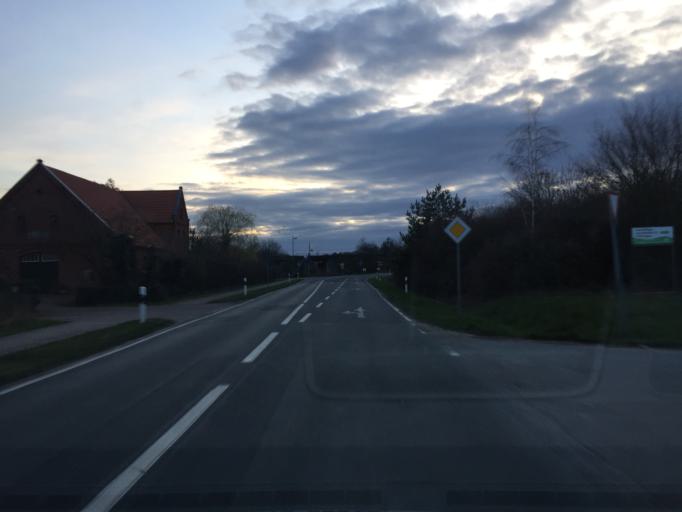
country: DE
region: Lower Saxony
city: Steimbke
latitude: 52.5750
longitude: 9.4097
